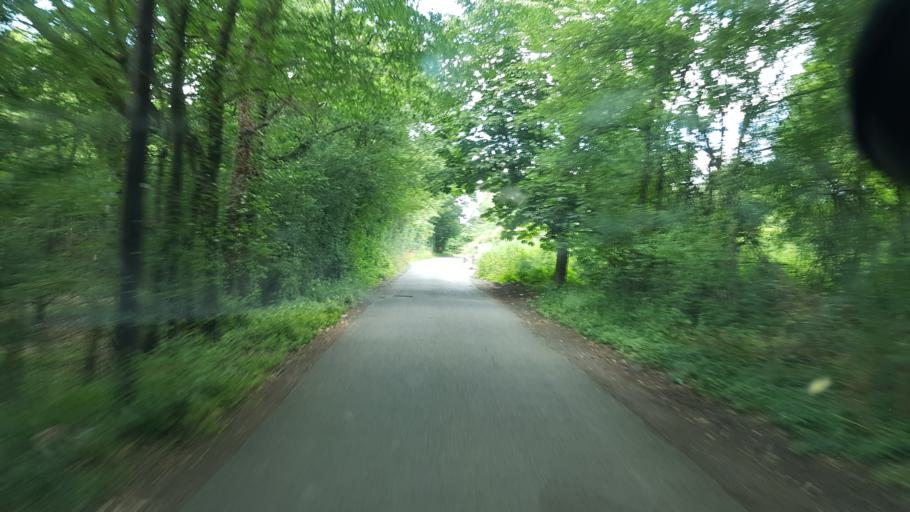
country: GB
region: England
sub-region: West Sussex
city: Billingshurst
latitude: 51.0293
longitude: -0.4312
